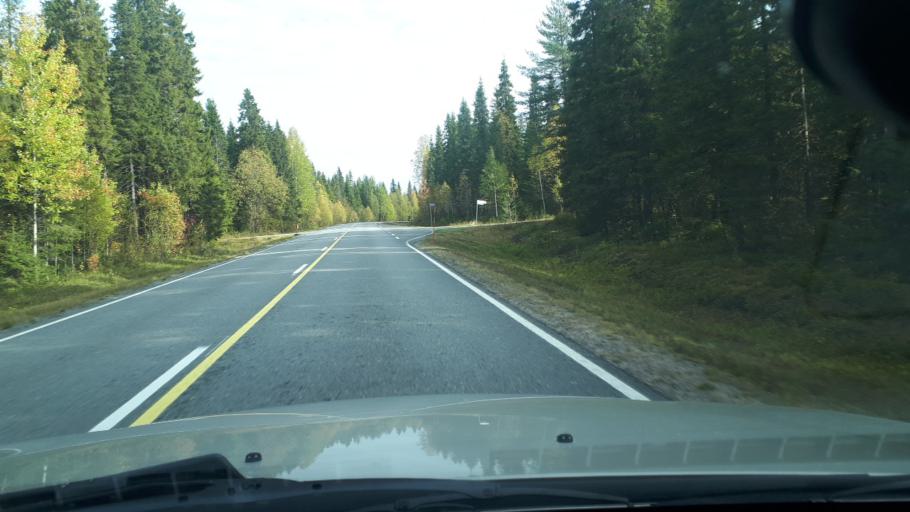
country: FI
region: Northern Ostrobothnia
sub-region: Oulu
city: Yli-Ii
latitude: 65.9496
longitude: 25.9081
